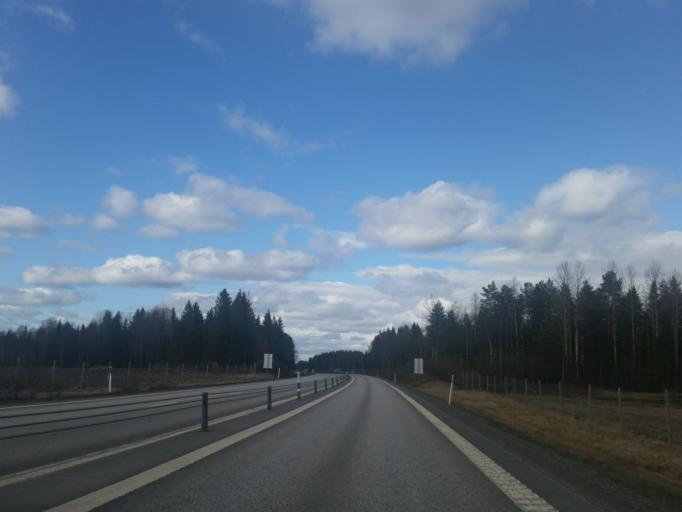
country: SE
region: Vaesterbotten
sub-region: Robertsfors Kommun
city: Robertsfors
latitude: 64.0828
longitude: 20.8677
